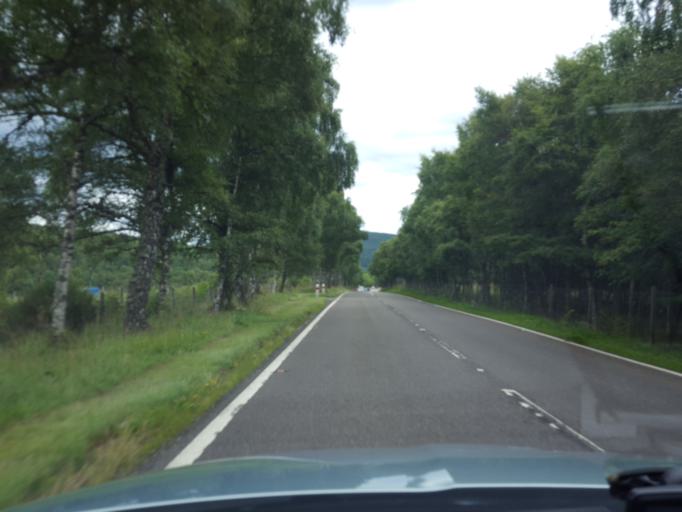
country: GB
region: Scotland
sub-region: Highland
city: Grantown on Spey
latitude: 57.3699
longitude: -3.4965
